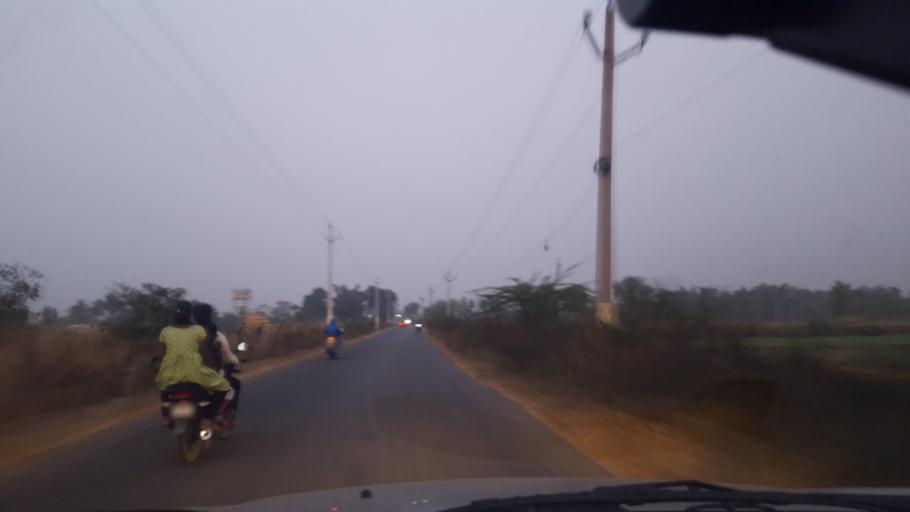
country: IN
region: Andhra Pradesh
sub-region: Srikakulam
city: Palasa
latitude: 18.7317
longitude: 84.3970
